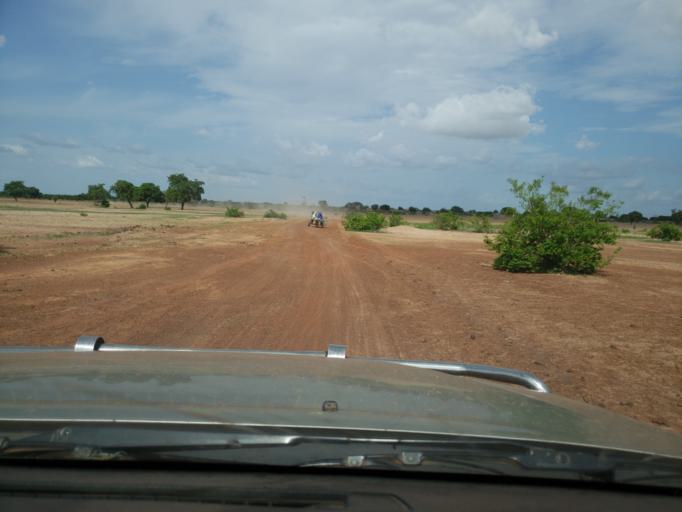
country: ML
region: Segou
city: Bla
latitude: 12.7433
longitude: -5.6400
